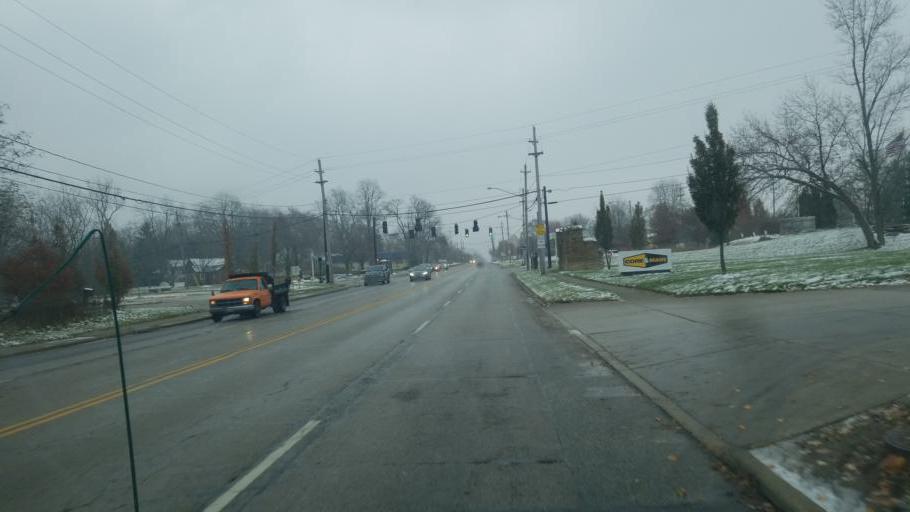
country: US
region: Ohio
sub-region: Cuyahoga County
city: Oakwood
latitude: 41.3659
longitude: -81.5090
